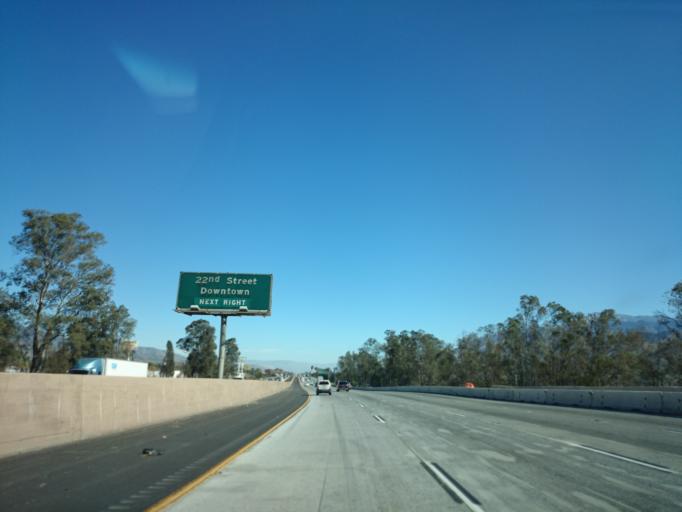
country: US
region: California
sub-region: Riverside County
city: Banning
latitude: 33.9242
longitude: -116.9102
